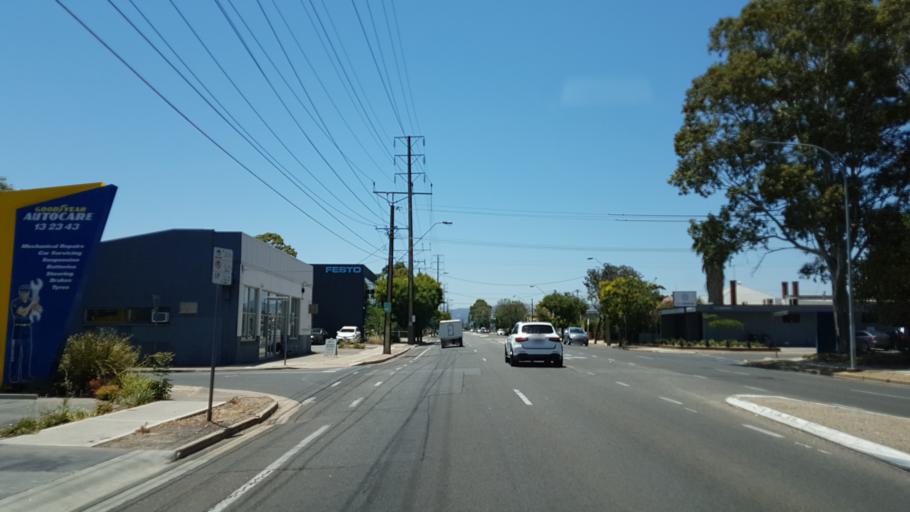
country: AU
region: South Australia
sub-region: City of West Torrens
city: Plympton
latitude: -34.9428
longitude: 138.5565
